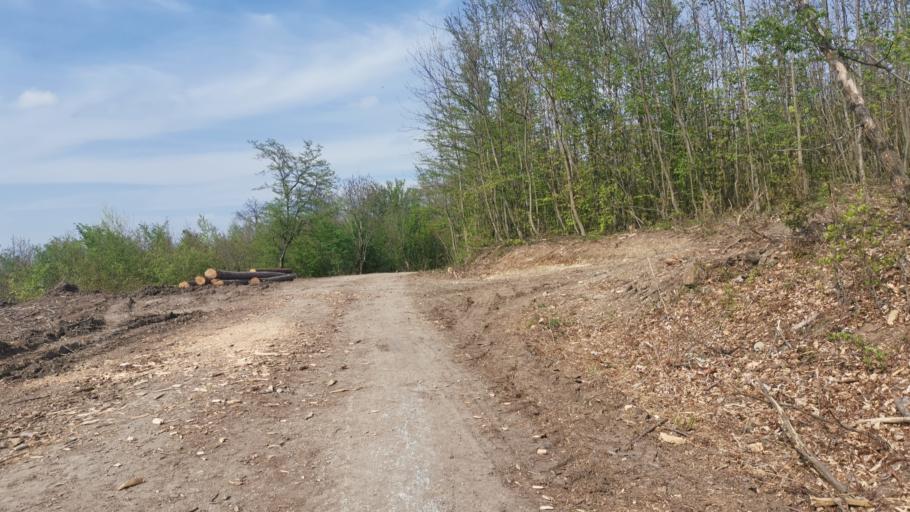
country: SK
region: Trnavsky
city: Smolenice
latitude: 48.5655
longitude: 17.3578
